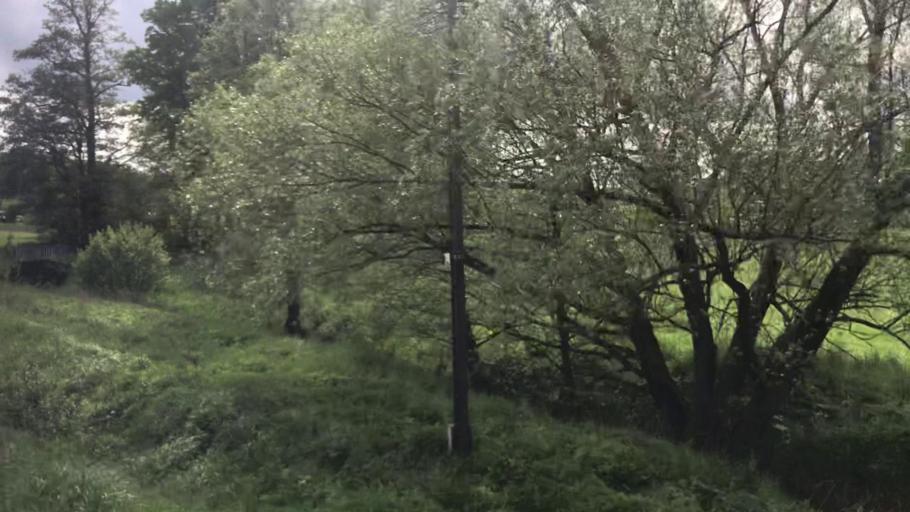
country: PL
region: Lower Silesian Voivodeship
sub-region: Powiat swidnicki
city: Swiebodzice
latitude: 50.8342
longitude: 16.3435
